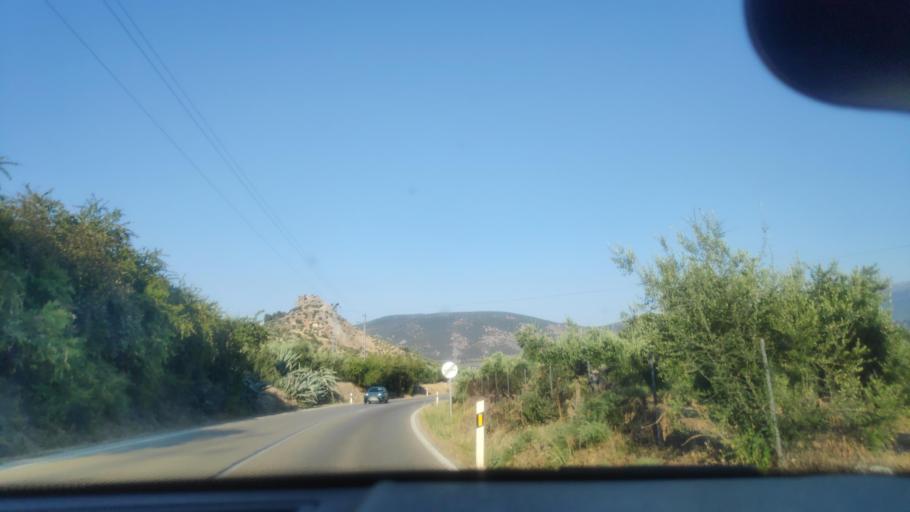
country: ES
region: Andalusia
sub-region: Provincia de Jaen
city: Jaen
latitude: 37.7476
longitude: -3.7845
